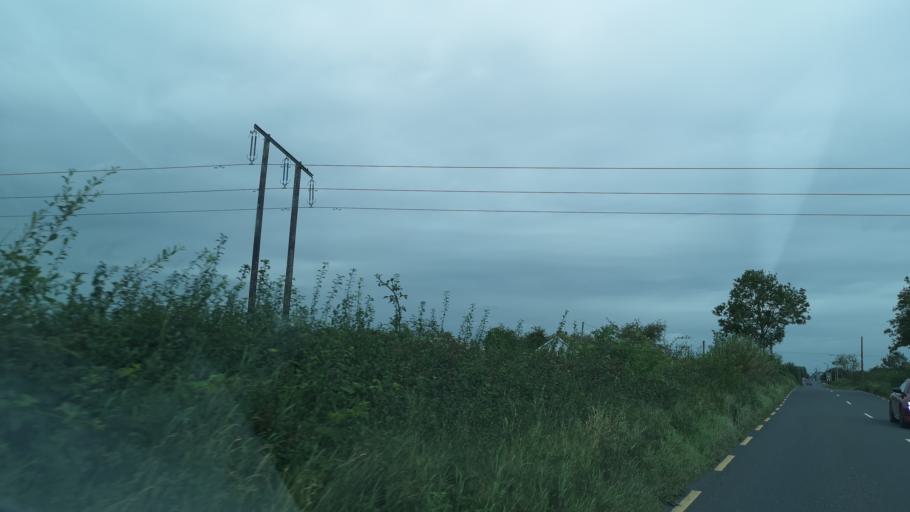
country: IE
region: Leinster
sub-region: Uibh Fhaili
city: Ferbane
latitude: 53.2185
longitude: -7.8933
